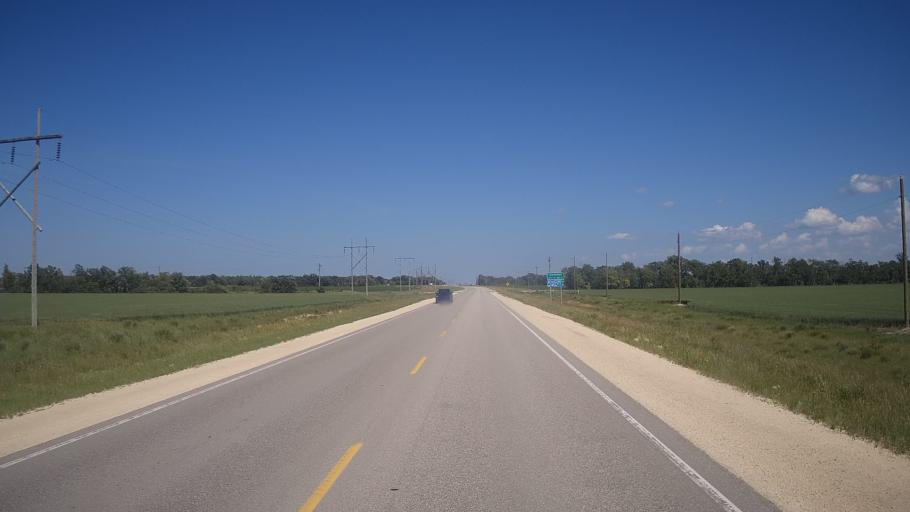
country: CA
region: Manitoba
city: Stonewall
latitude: 50.1228
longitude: -97.3488
